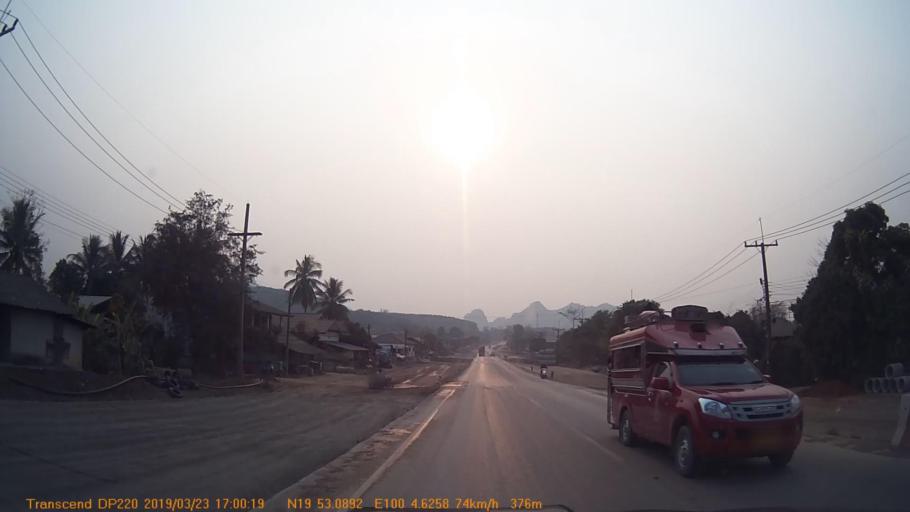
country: TH
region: Chiang Rai
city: Phaya Mengrai
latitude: 19.8848
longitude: 100.0767
